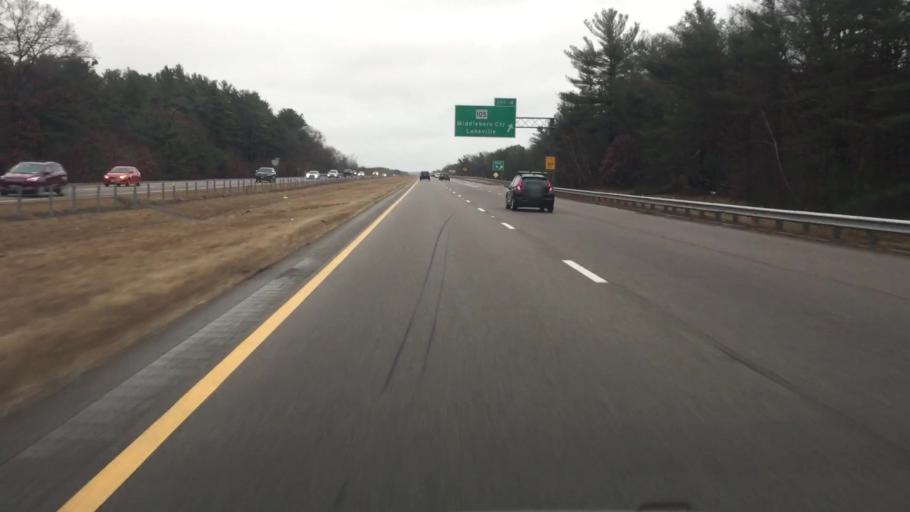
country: US
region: Massachusetts
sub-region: Plymouth County
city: Middleborough Center
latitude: 41.8842
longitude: -70.9256
